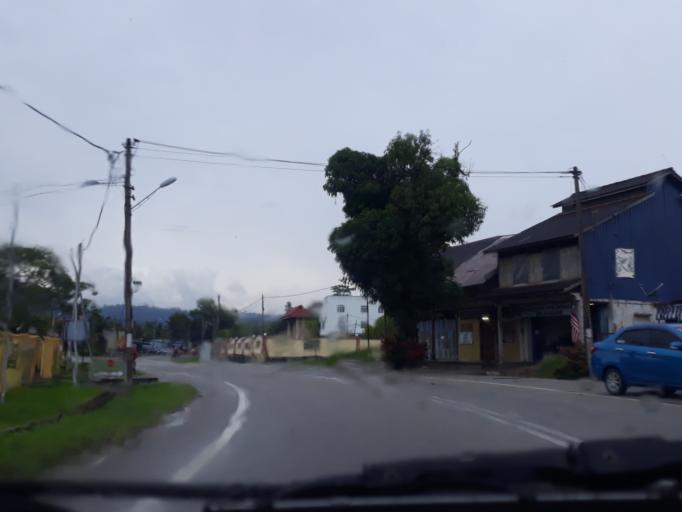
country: MY
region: Penang
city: Nibong Tebal
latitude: 5.2134
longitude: 100.6128
